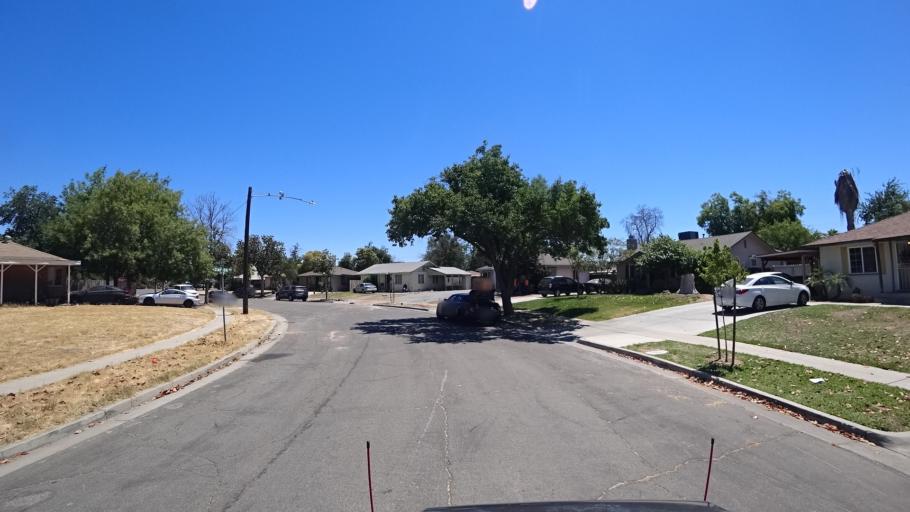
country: US
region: California
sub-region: Fresno County
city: Fresno
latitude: 36.7784
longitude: -119.8211
